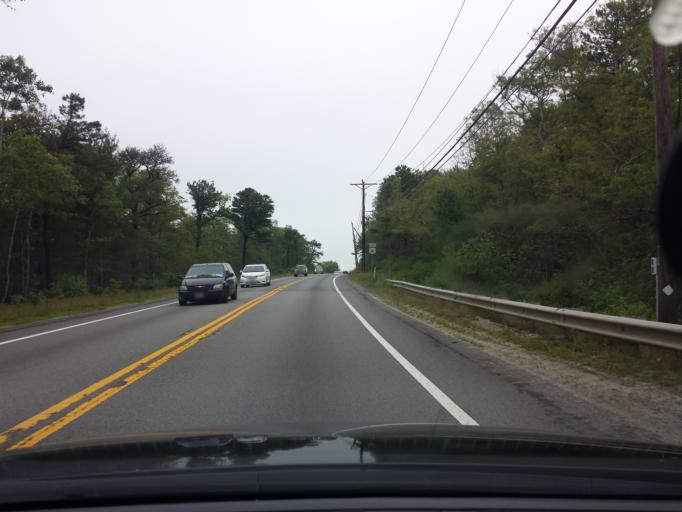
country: US
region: Massachusetts
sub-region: Barnstable County
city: Bourne
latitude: 41.7512
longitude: -70.5769
